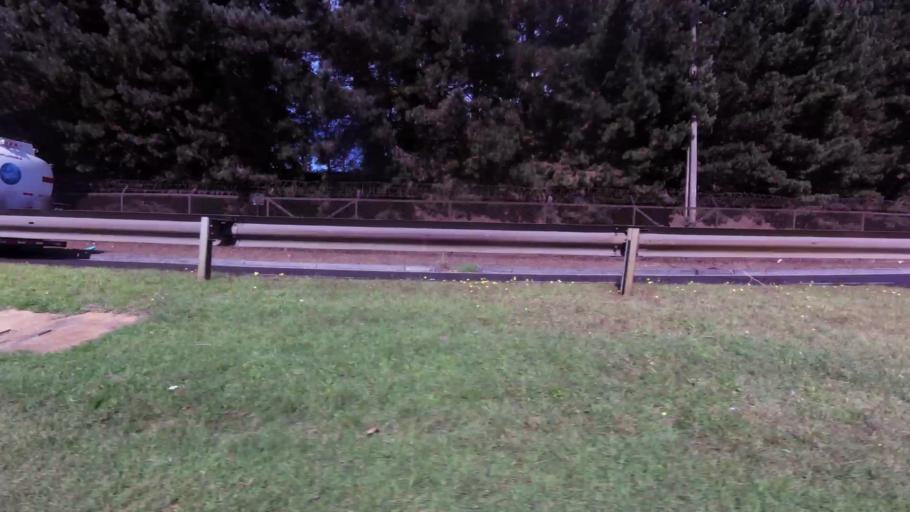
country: CL
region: Biobio
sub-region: Provincia de Concepcion
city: Talcahuano
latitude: -36.7504
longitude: -73.1235
